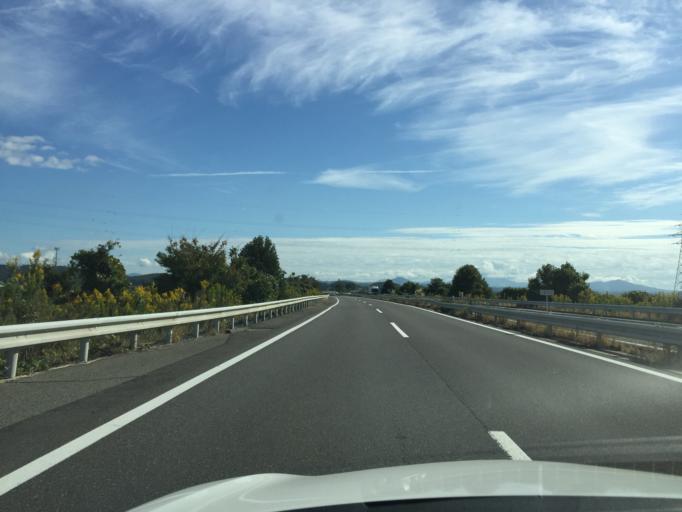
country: JP
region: Fukushima
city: Motomiya
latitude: 37.4625
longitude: 140.3632
